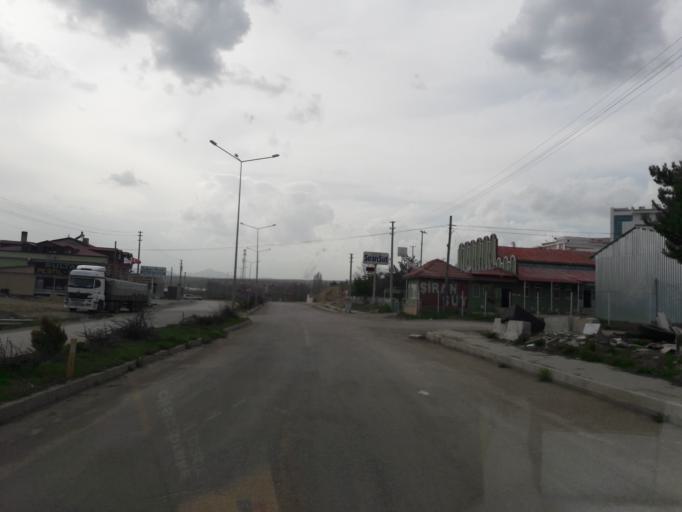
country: TR
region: Gumushane
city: Siran
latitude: 40.1784
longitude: 39.1254
